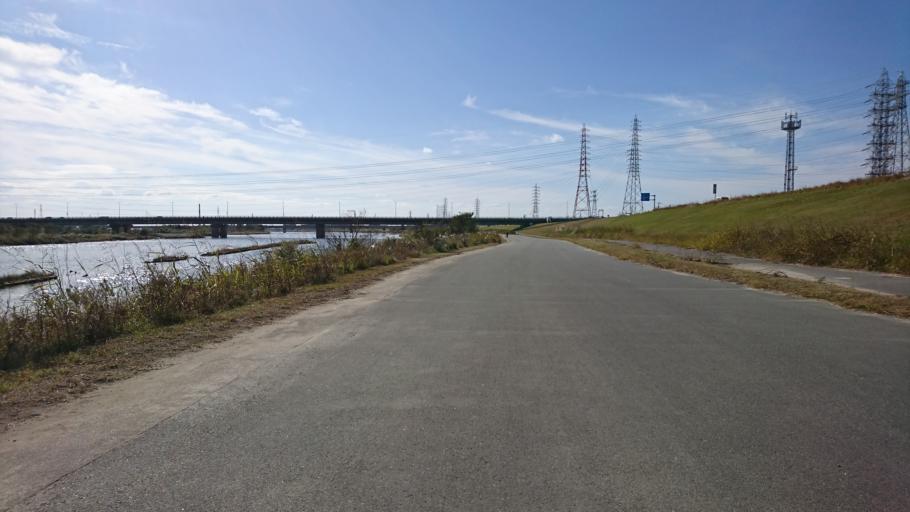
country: JP
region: Hyogo
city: Kakogawacho-honmachi
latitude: 34.7691
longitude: 134.8104
